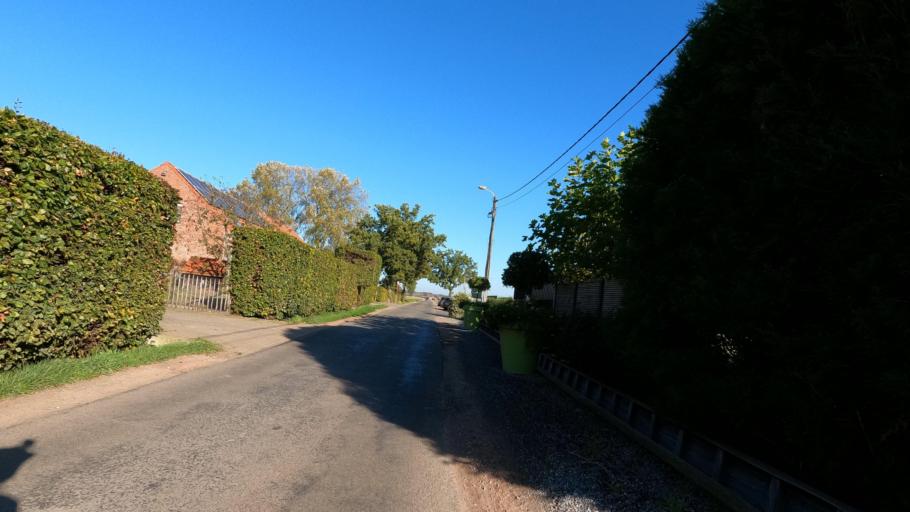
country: BE
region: Flanders
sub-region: Provincie Antwerpen
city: Oostmalle
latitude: 51.3134
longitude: 4.7492
